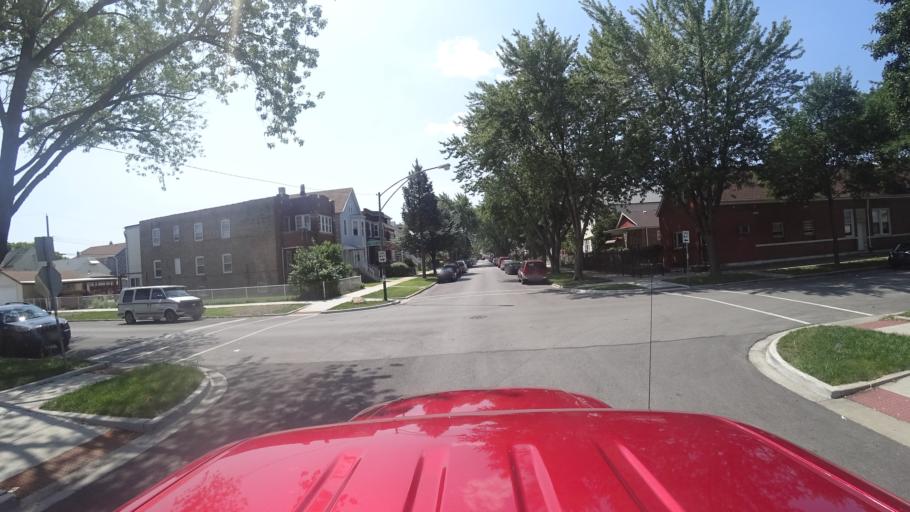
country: US
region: Illinois
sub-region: Cook County
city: Cicero
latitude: 41.7993
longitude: -87.7001
